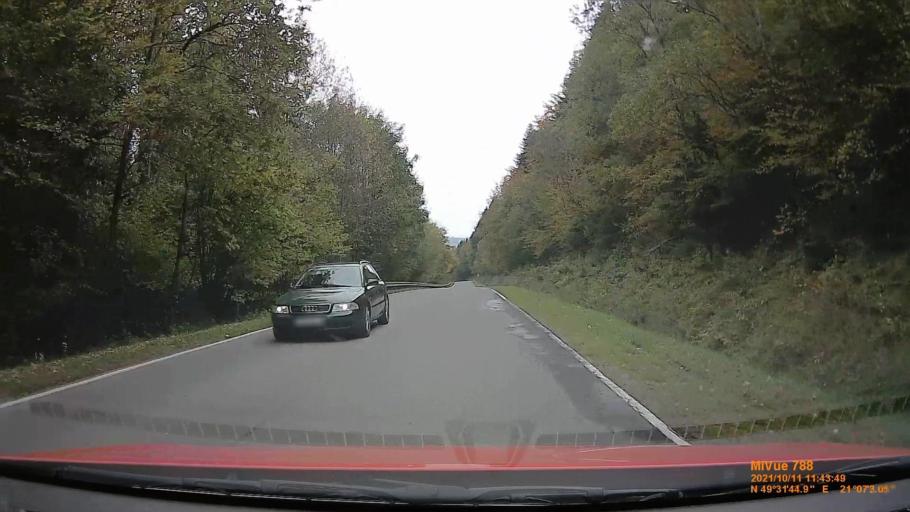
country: PL
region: Lesser Poland Voivodeship
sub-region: Powiat gorlicki
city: Uscie Gorlickie
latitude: 49.5291
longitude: 21.1178
